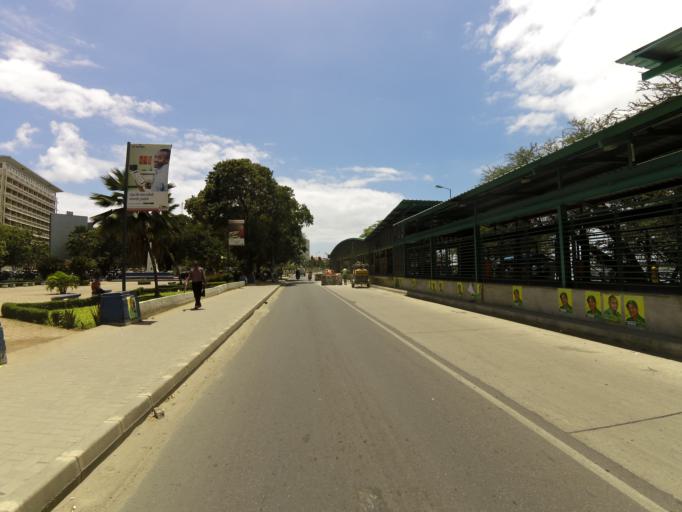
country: TZ
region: Dar es Salaam
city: Dar es Salaam
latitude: -6.8185
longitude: 39.2900
